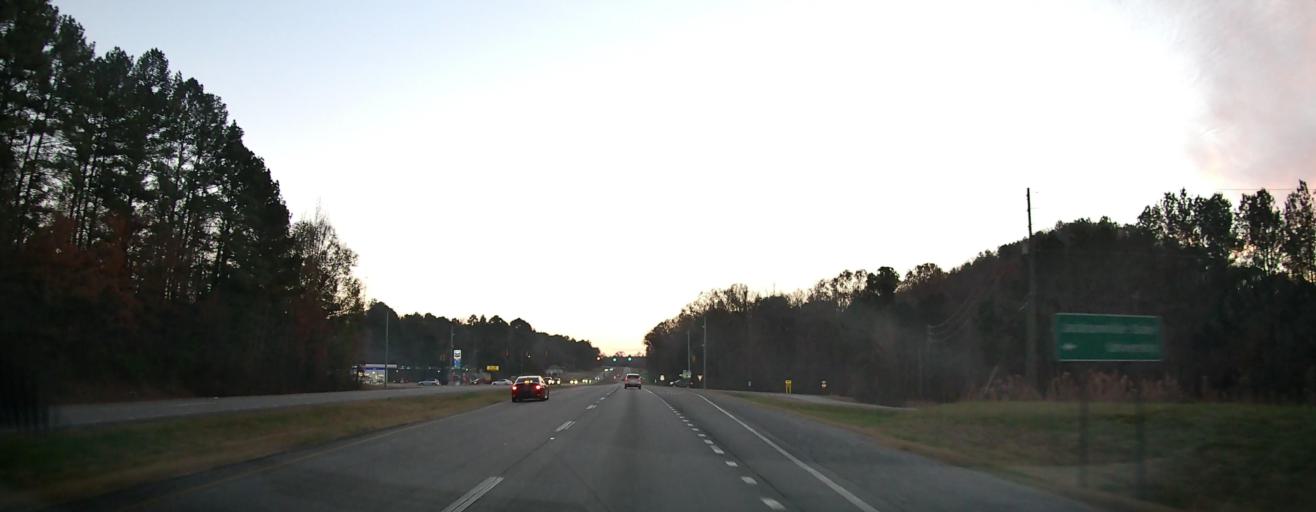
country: US
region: Alabama
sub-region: Calhoun County
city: Alexandria
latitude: 33.8547
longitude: -85.9158
